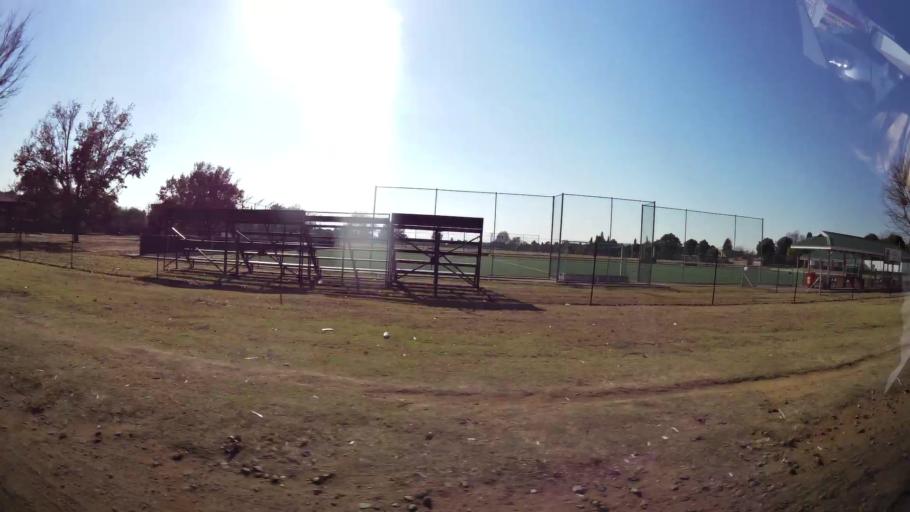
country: ZA
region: Gauteng
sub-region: Ekurhuleni Metropolitan Municipality
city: Benoni
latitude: -26.1502
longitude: 28.3158
